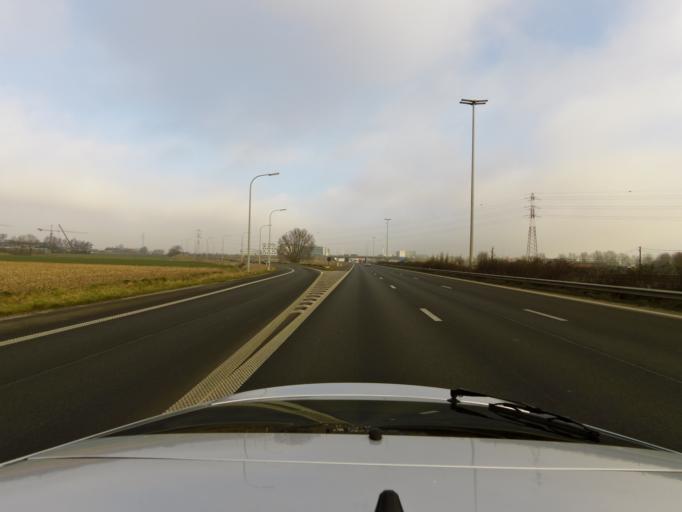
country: BE
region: Flanders
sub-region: Provincie West-Vlaanderen
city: Izegem
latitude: 50.9152
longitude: 3.1778
